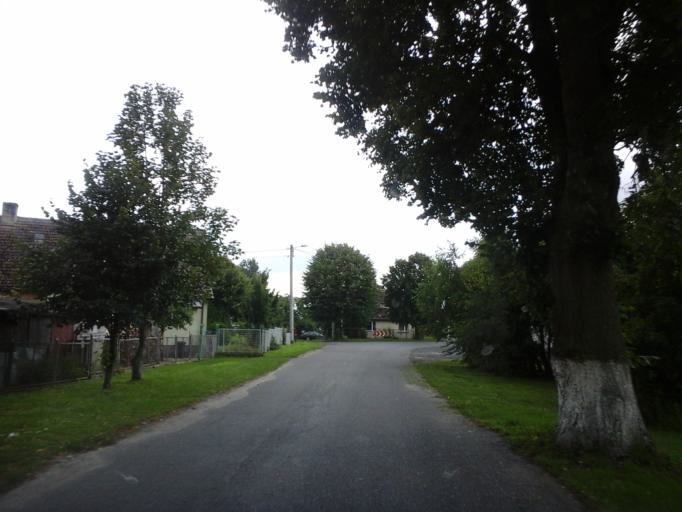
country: PL
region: West Pomeranian Voivodeship
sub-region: Powiat choszczenski
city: Krzecin
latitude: 53.0552
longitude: 15.4763
